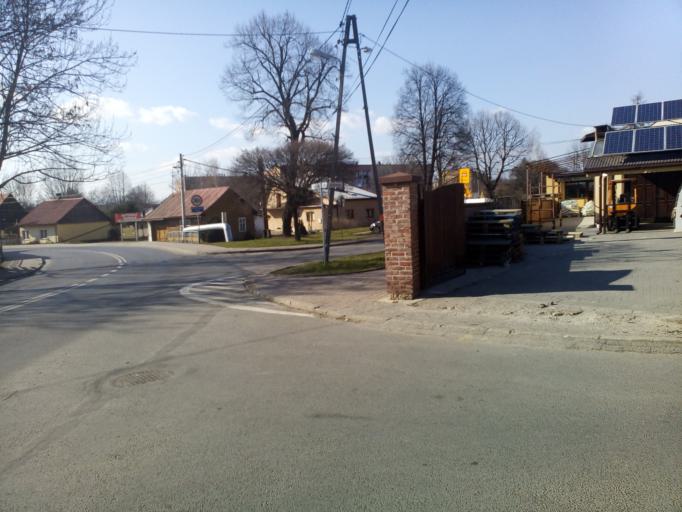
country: PL
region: Lesser Poland Voivodeship
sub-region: Powiat nowosadecki
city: Stary Sacz
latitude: 49.5661
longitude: 20.6302
